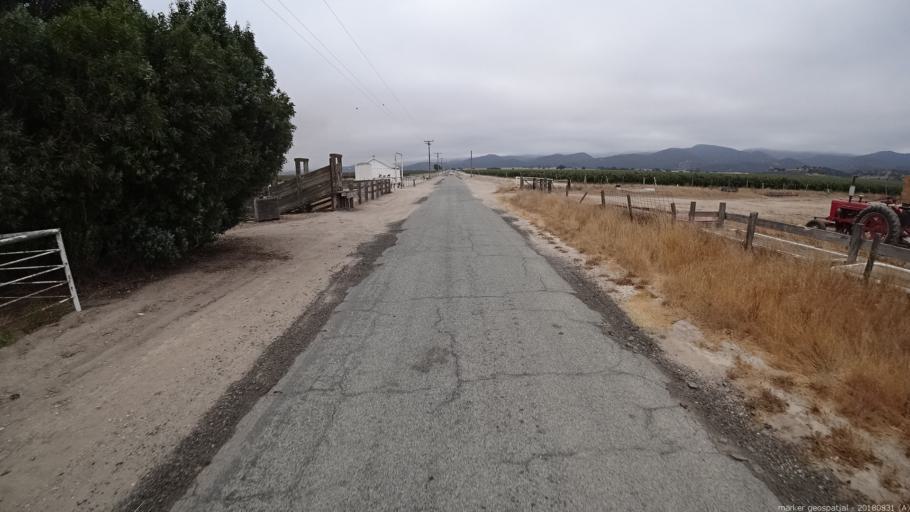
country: US
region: California
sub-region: Monterey County
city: King City
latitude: 36.1221
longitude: -121.0875
